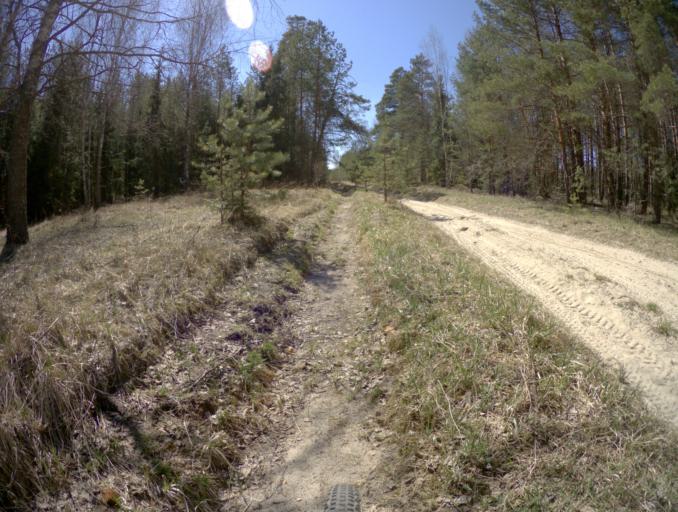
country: RU
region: Vladimir
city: Golovino
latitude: 55.8839
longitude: 40.4059
